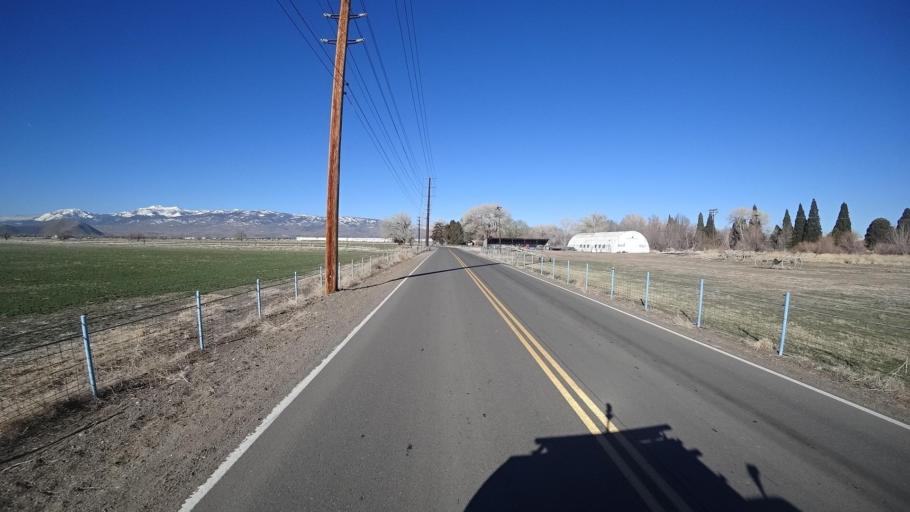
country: US
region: Nevada
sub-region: Washoe County
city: Sparks
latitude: 39.5115
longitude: -119.7294
